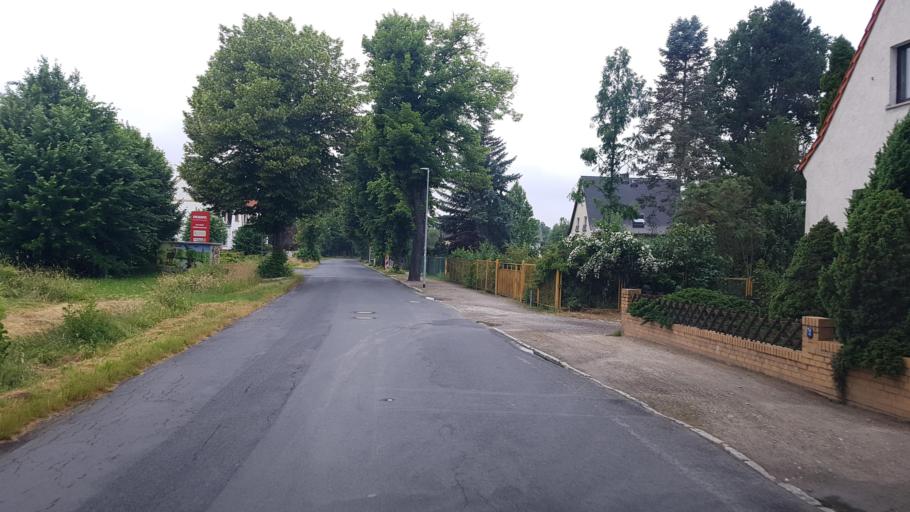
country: DE
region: Brandenburg
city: Ortrand
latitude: 51.3755
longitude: 13.7535
